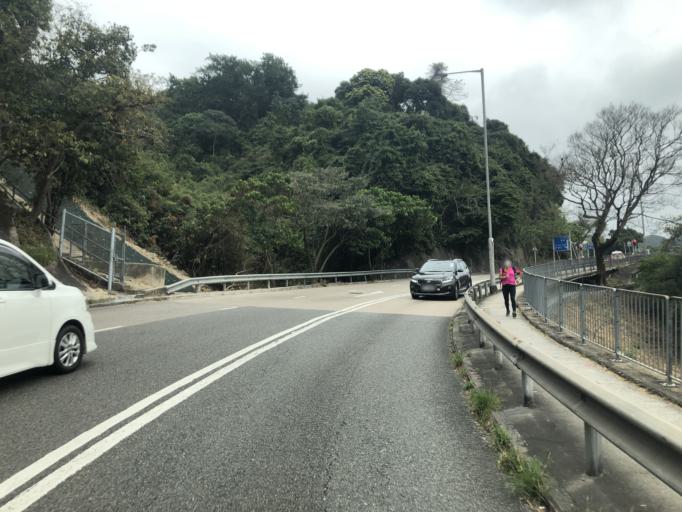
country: HK
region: Wong Tai Sin
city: Wong Tai Sin
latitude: 22.3345
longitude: 114.2240
